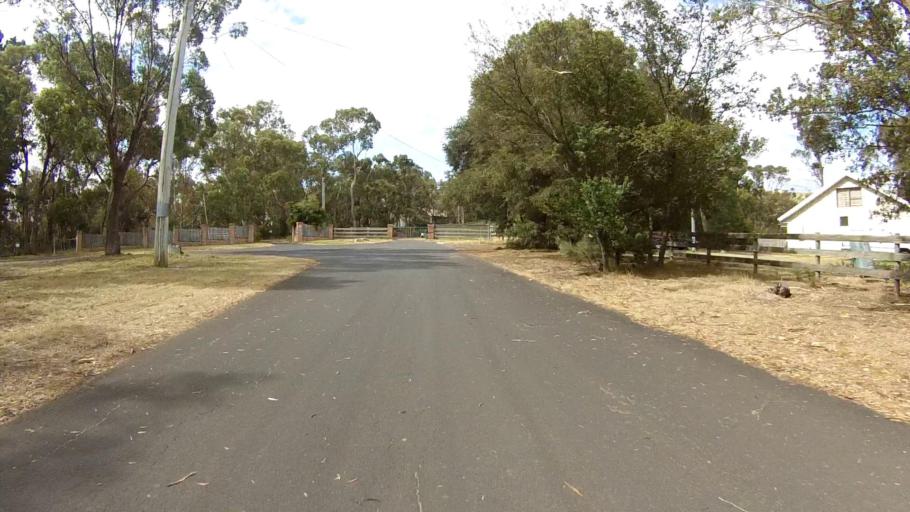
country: AU
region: Tasmania
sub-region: Clarence
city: Acton Park
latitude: -42.8810
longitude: 147.4923
